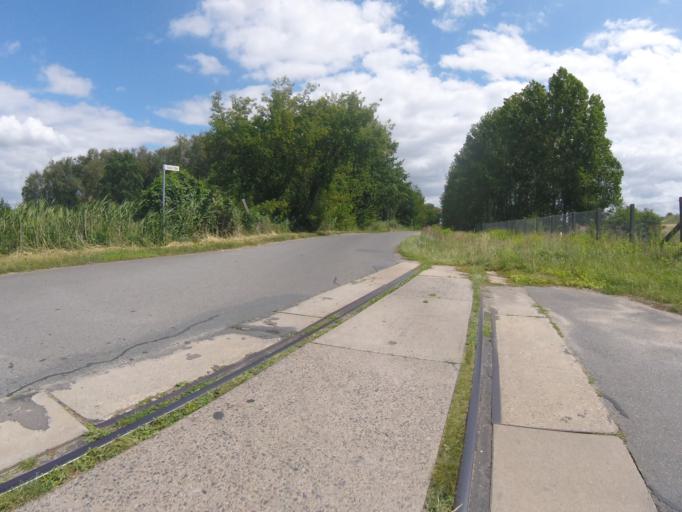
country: DE
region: Brandenburg
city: Mittenwalde
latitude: 52.2426
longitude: 13.5211
